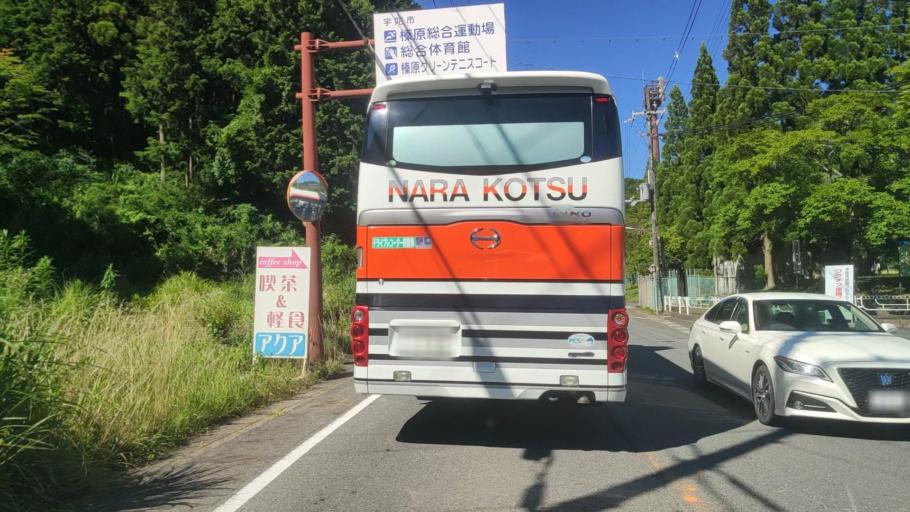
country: JP
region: Nara
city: Haibara-akanedai
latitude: 34.5411
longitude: 135.9564
